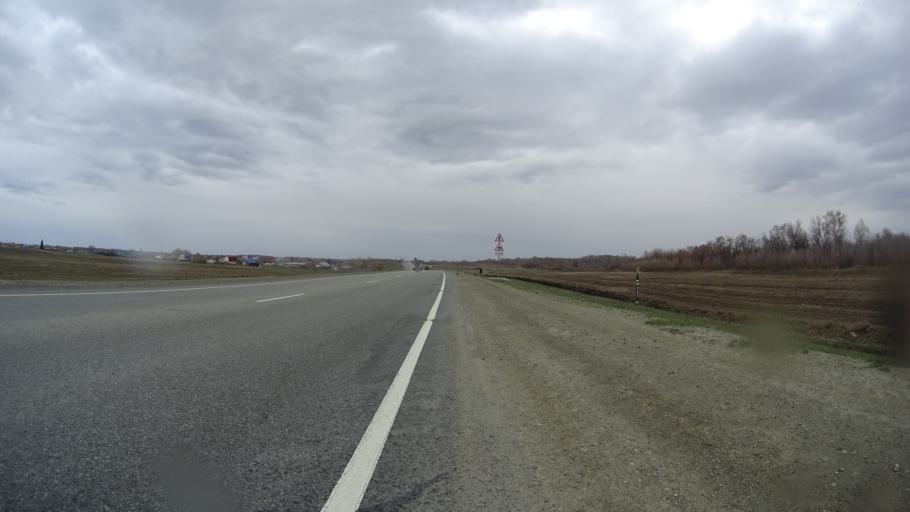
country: RU
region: Chelyabinsk
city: Krasnogorskiy
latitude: 54.6789
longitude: 61.2472
